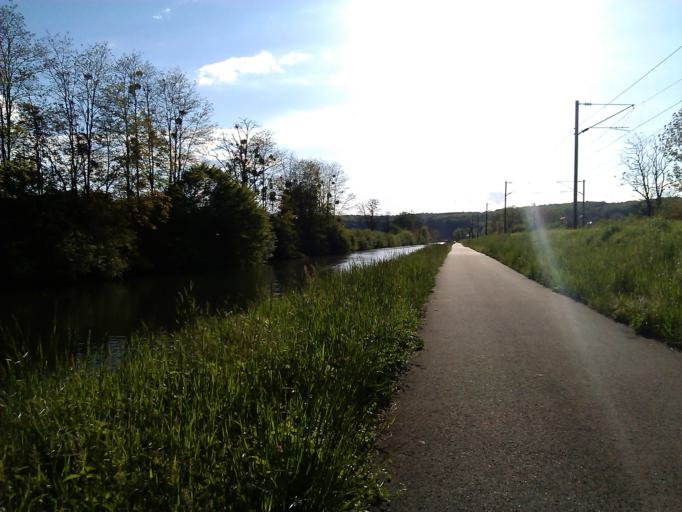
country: FR
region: Franche-Comte
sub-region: Departement du Doubs
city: Clerval
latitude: 47.4161
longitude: 6.5336
